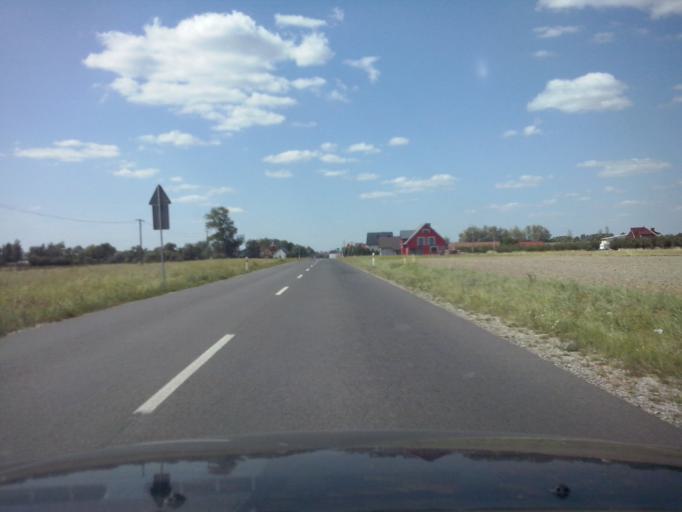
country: PL
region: Swietokrzyskie
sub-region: Powiat buski
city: Gnojno
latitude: 50.5977
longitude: 20.8715
